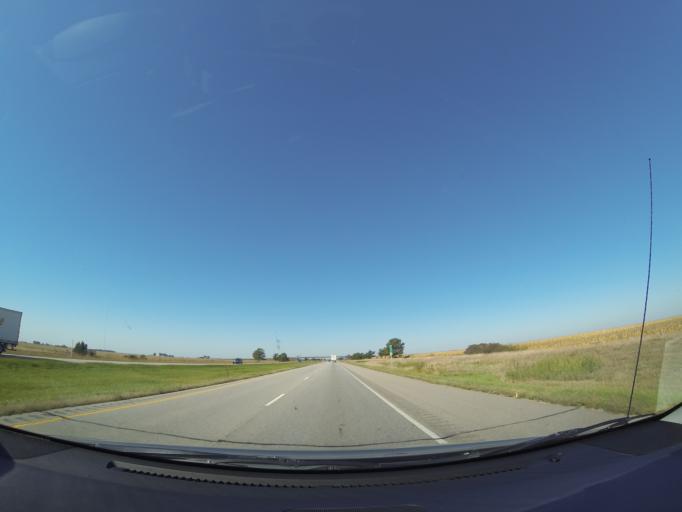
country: US
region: Nebraska
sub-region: Seward County
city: Seward
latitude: 40.8225
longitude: -97.1531
